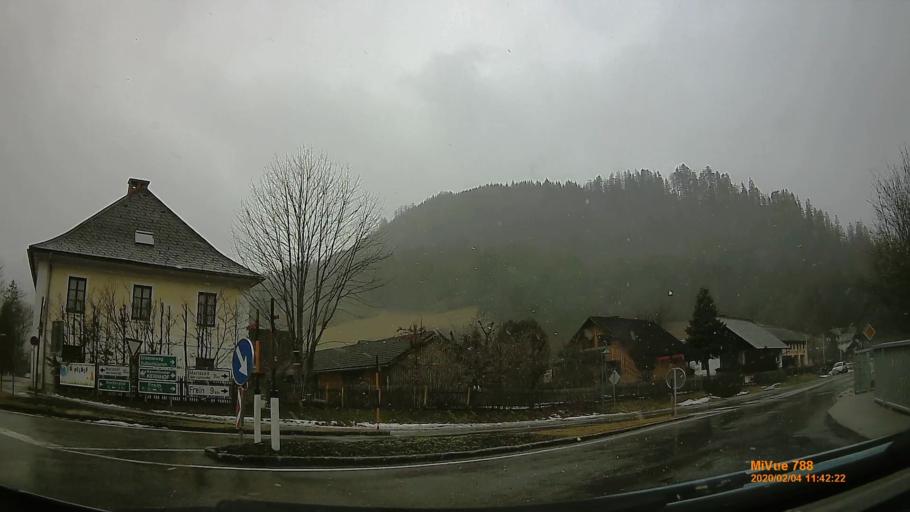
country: AT
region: Styria
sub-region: Politischer Bezirk Bruck-Muerzzuschlag
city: Muerzsteg
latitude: 47.6757
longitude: 15.4920
